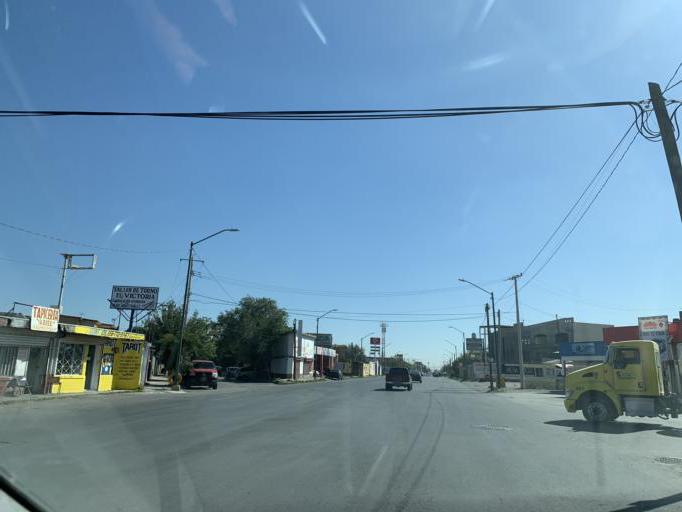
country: MX
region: Chihuahua
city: Ciudad Juarez
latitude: 31.7184
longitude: -106.4626
